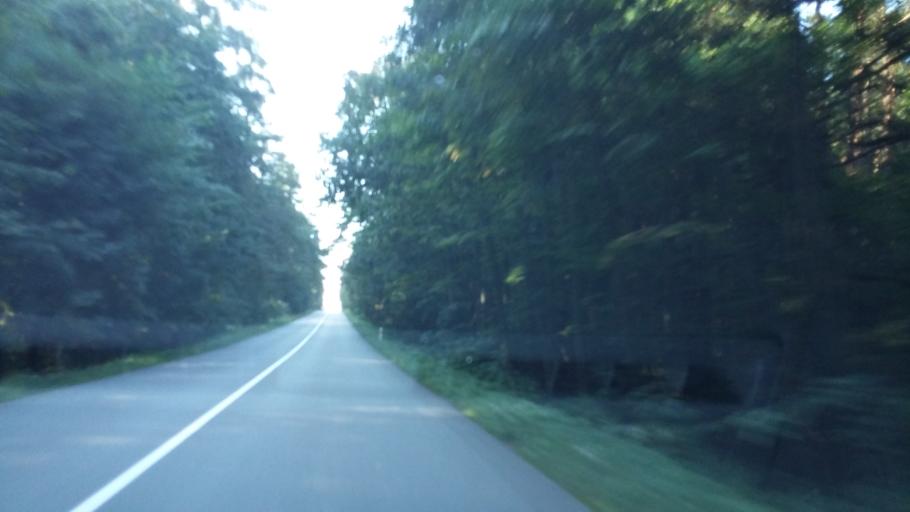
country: CZ
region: South Moravian
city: Ricany
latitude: 49.2237
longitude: 16.3654
